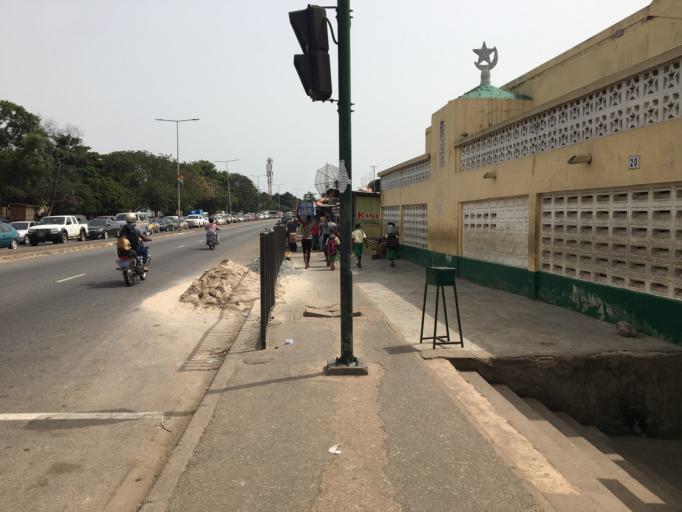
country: GH
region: Greater Accra
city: Accra
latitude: 5.5876
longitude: -0.1924
